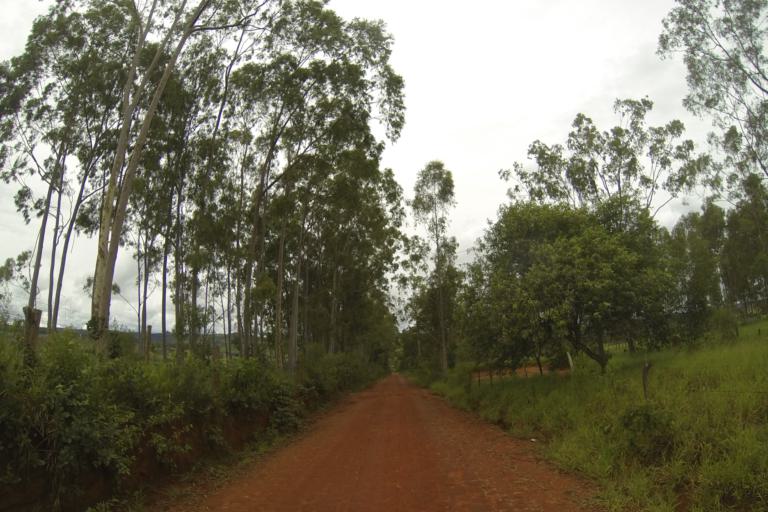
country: BR
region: Minas Gerais
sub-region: Ibia
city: Ibia
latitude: -19.6800
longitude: -46.6804
